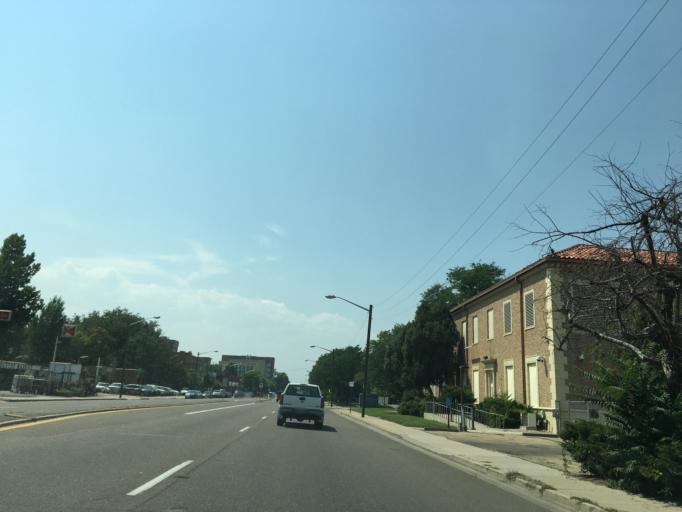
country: US
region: Colorado
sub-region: Arapahoe County
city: Glendale
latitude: 39.7402
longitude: -104.9361
